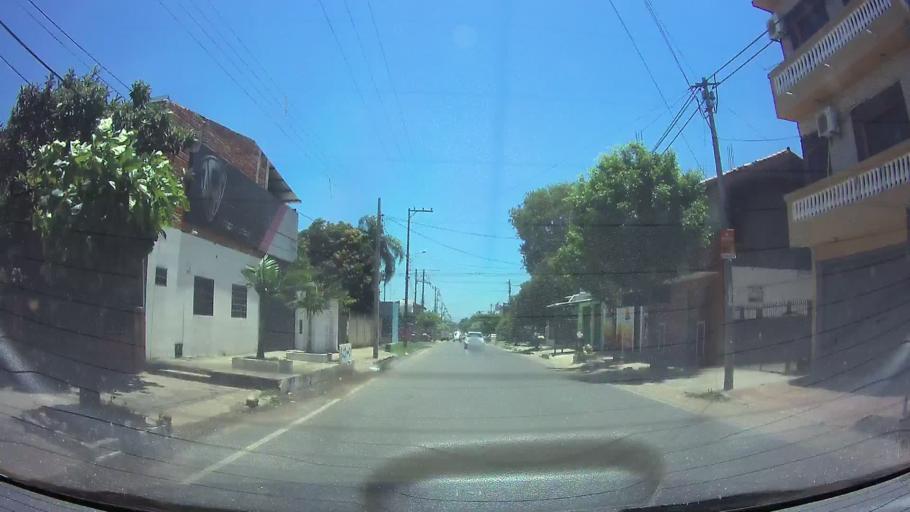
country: PY
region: Central
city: Fernando de la Mora
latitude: -25.2984
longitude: -57.5438
